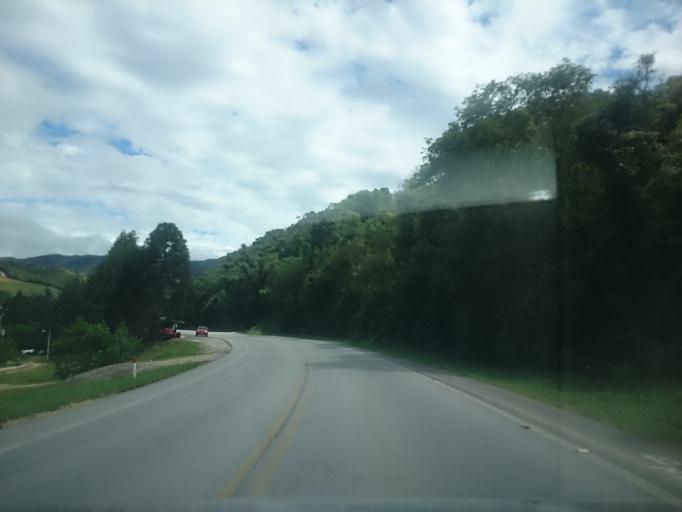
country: BR
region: Santa Catarina
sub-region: Anitapolis
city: Anitapolis
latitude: -27.7032
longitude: -49.2386
